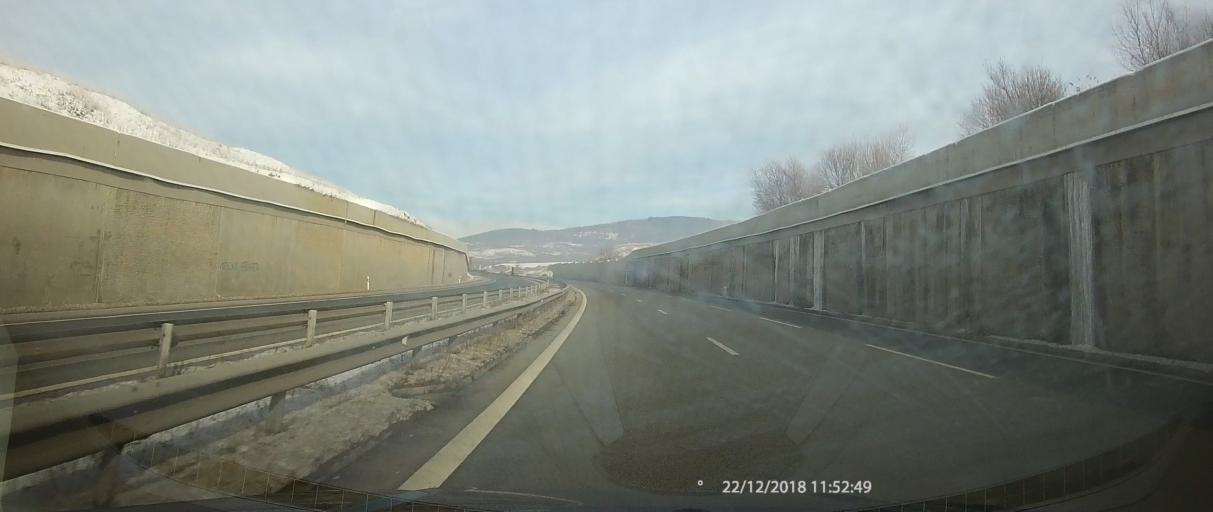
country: BG
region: Pernik
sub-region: Obshtina Pernik
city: Pernik
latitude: 42.6148
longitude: 23.1393
